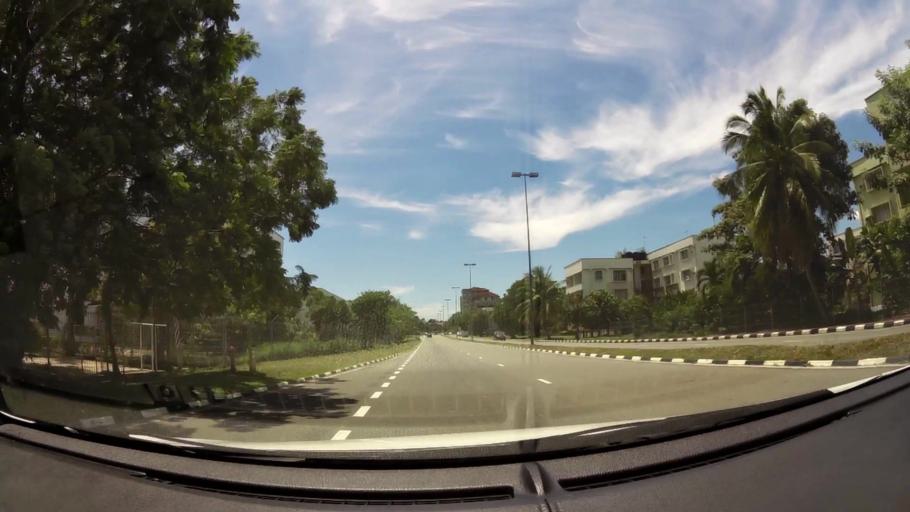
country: BN
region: Brunei and Muara
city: Bandar Seri Begawan
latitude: 4.9338
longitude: 114.9419
